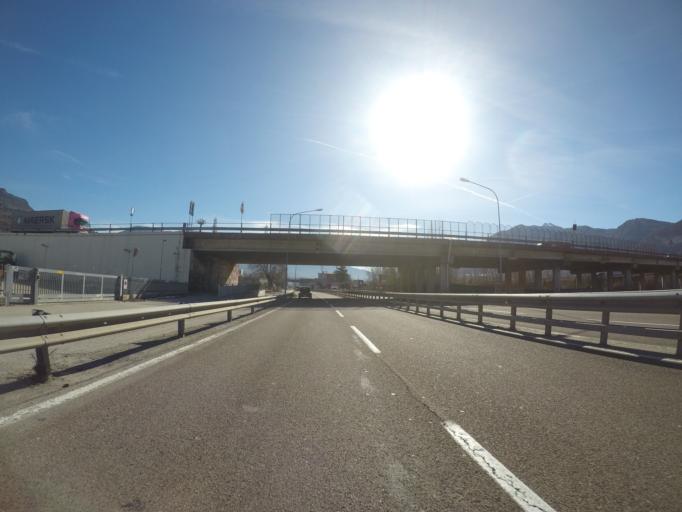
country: IT
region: Trentino-Alto Adige
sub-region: Provincia di Trento
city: Meano
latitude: 46.0964
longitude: 11.1128
